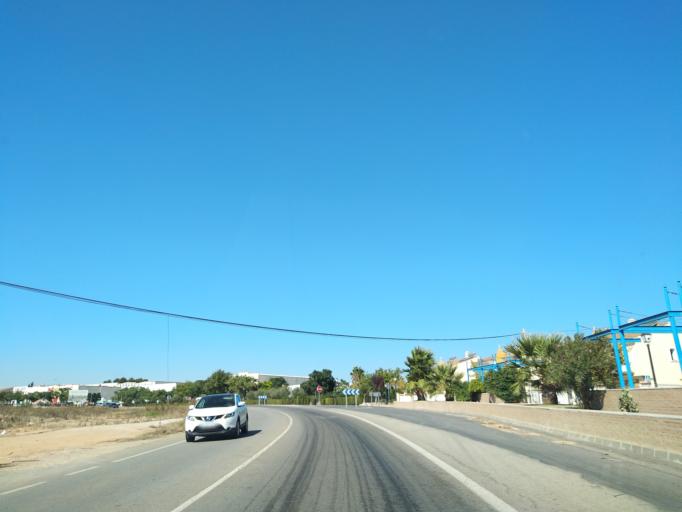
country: ES
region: Andalusia
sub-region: Provincia de Malaga
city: Mollina
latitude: 37.1202
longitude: -4.6610
